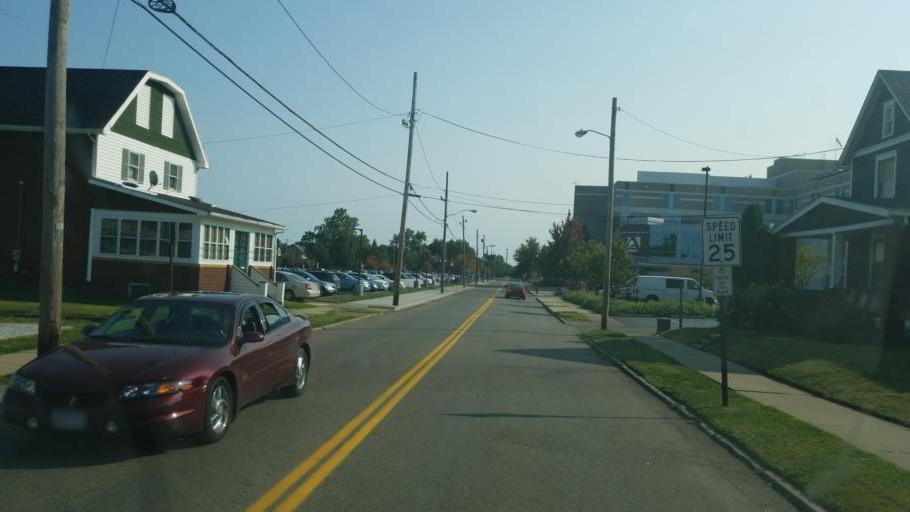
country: US
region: Ohio
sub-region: Stark County
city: Canton
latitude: 40.7988
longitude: -81.4022
